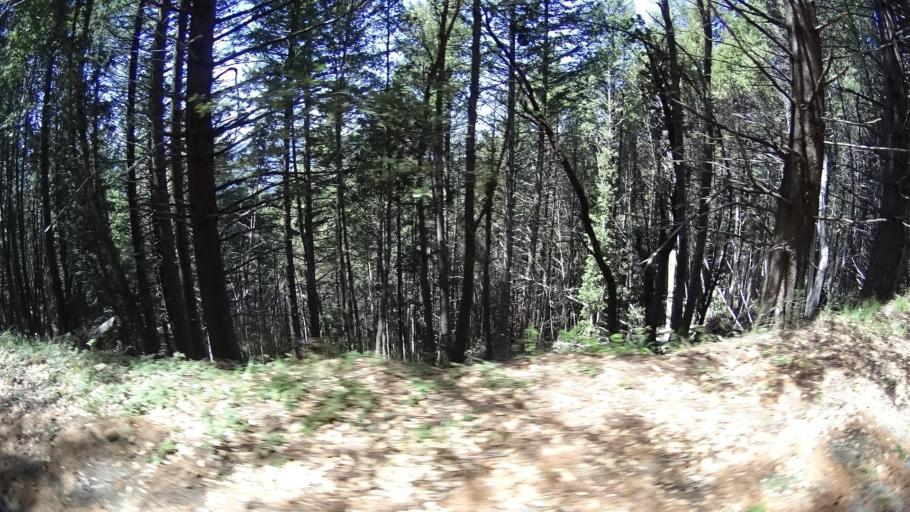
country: US
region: California
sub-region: Humboldt County
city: Rio Dell
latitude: 40.2657
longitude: -124.0895
